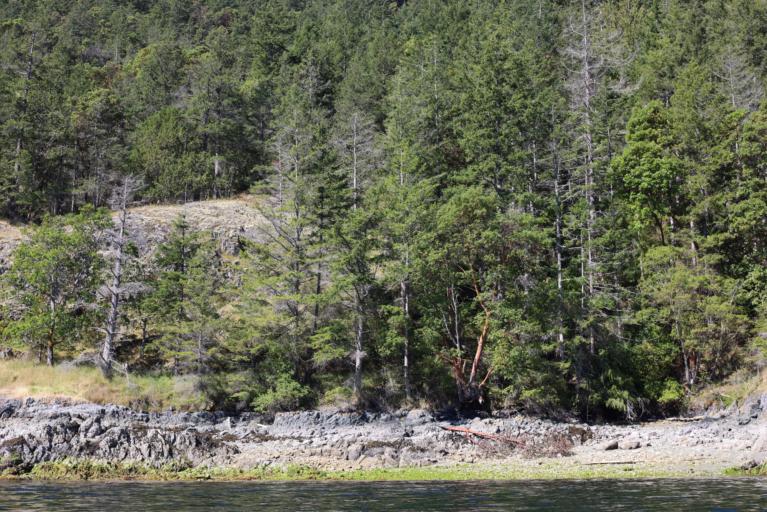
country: CA
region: British Columbia
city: North Cowichan
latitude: 48.8346
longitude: -123.5882
